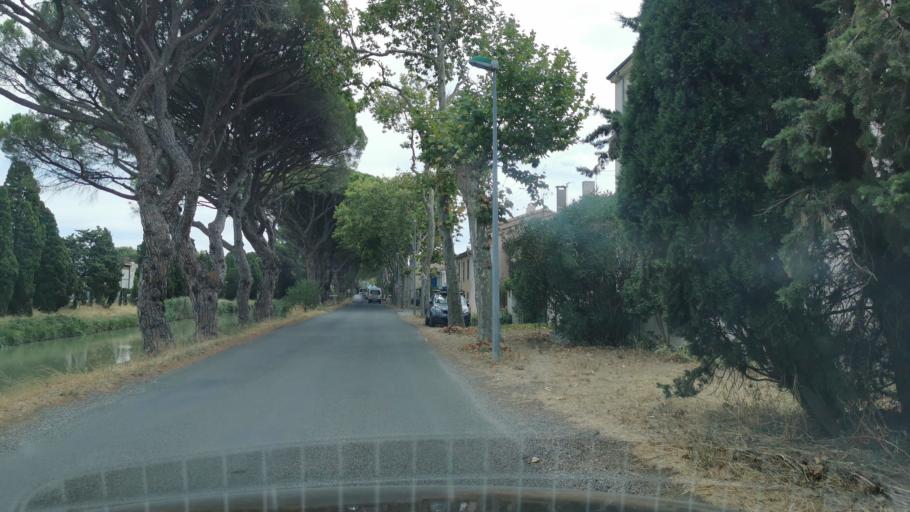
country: FR
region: Languedoc-Roussillon
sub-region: Departement de l'Aude
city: Saint-Marcel-sur-Aude
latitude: 43.2624
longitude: 2.9443
